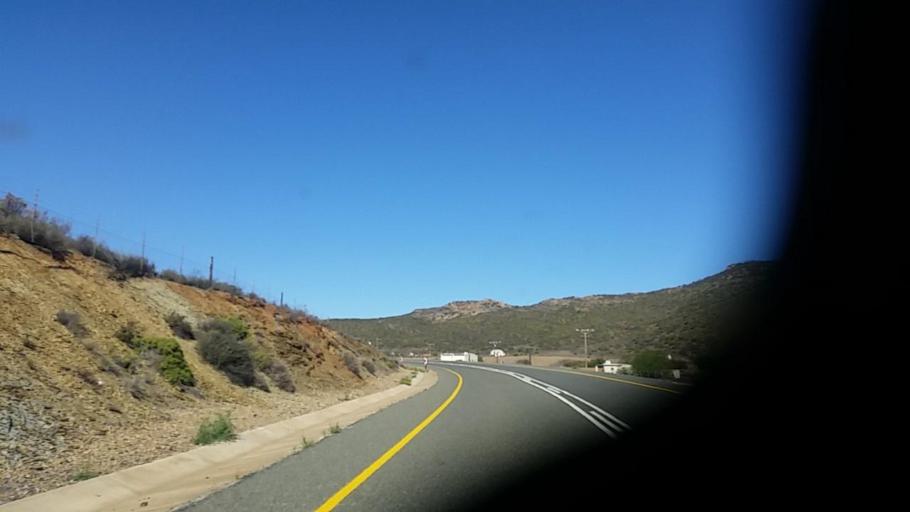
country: ZA
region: Western Cape
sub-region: Eden District Municipality
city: Knysna
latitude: -33.5347
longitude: 22.8981
